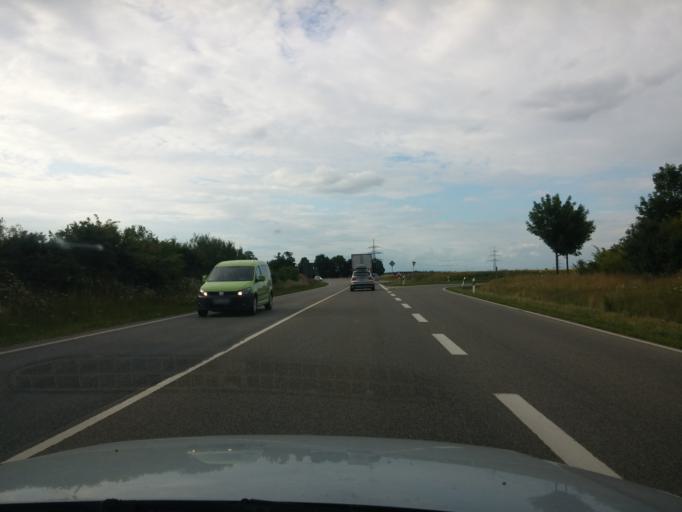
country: DE
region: Bavaria
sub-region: Upper Bavaria
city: Zorneding
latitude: 48.0810
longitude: 11.8098
